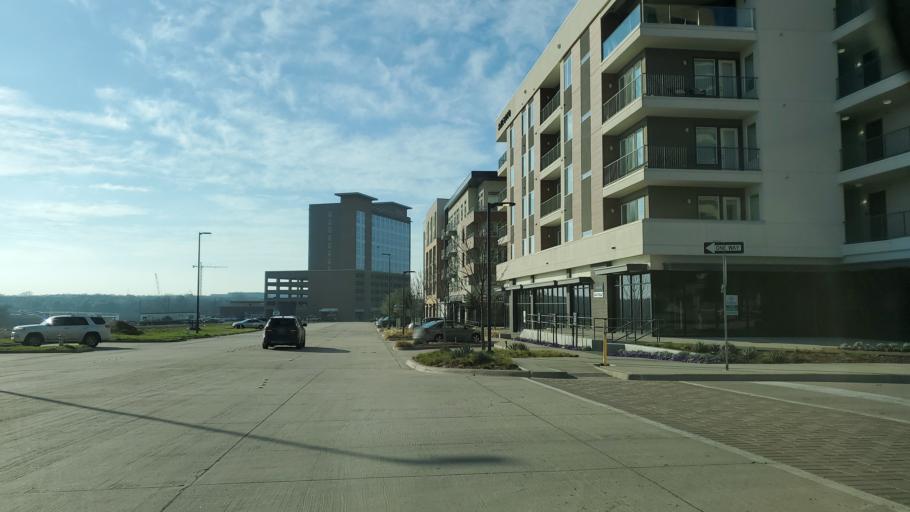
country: US
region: Texas
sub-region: Collin County
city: Plano
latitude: 33.0016
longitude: -96.7040
